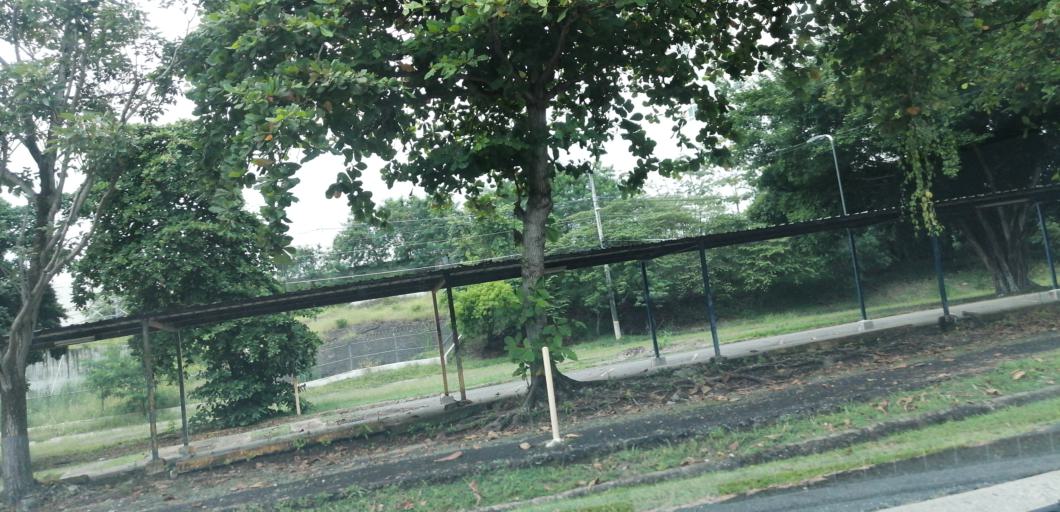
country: PA
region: Panama
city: Panama
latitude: 9.0280
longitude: -79.5210
